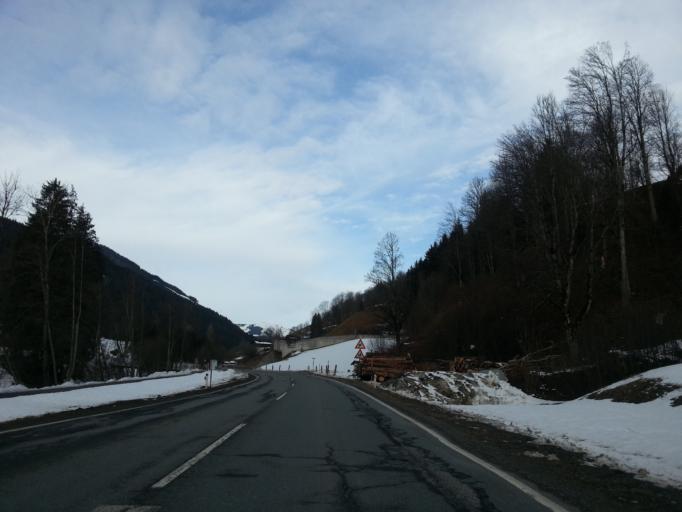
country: AT
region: Salzburg
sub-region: Politischer Bezirk Zell am See
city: Viehhofen
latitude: 47.3676
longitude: 12.7086
